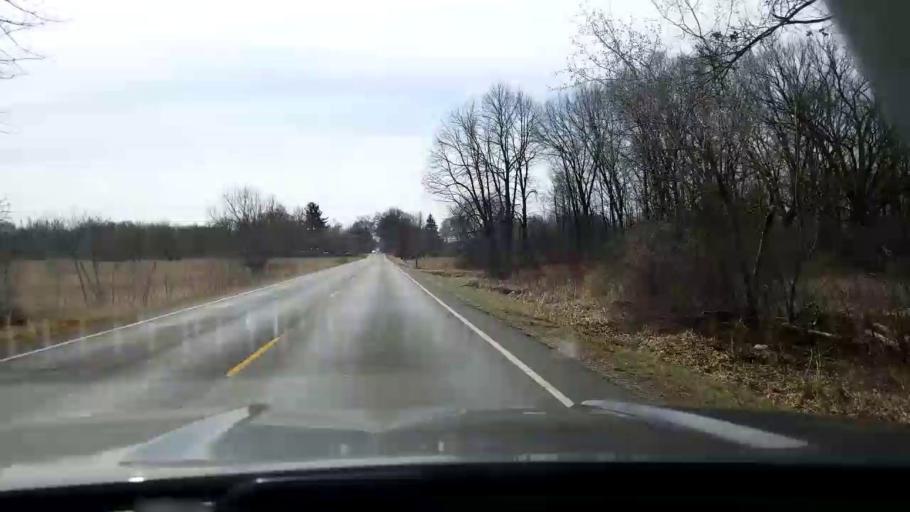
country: US
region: Michigan
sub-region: Jackson County
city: Spring Arbor
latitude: 42.2060
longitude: -84.5212
